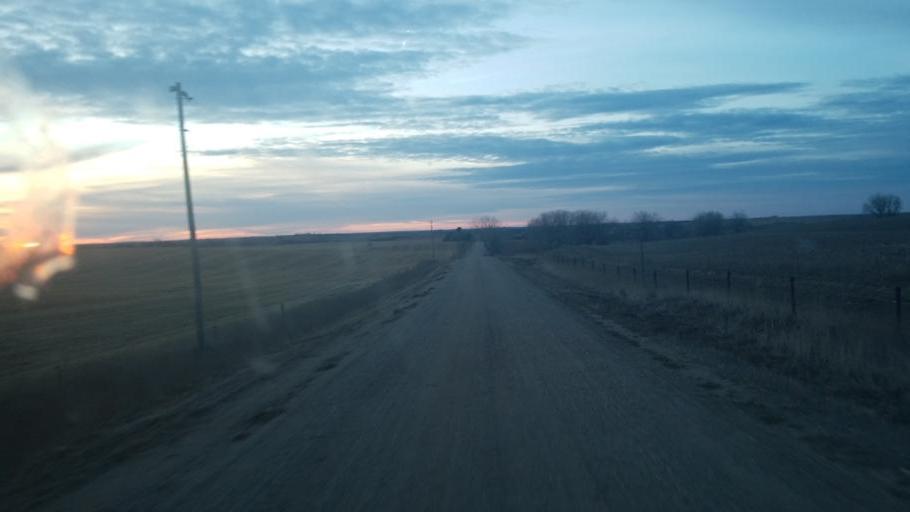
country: US
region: Nebraska
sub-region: Knox County
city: Center
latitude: 42.6554
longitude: -97.7624
